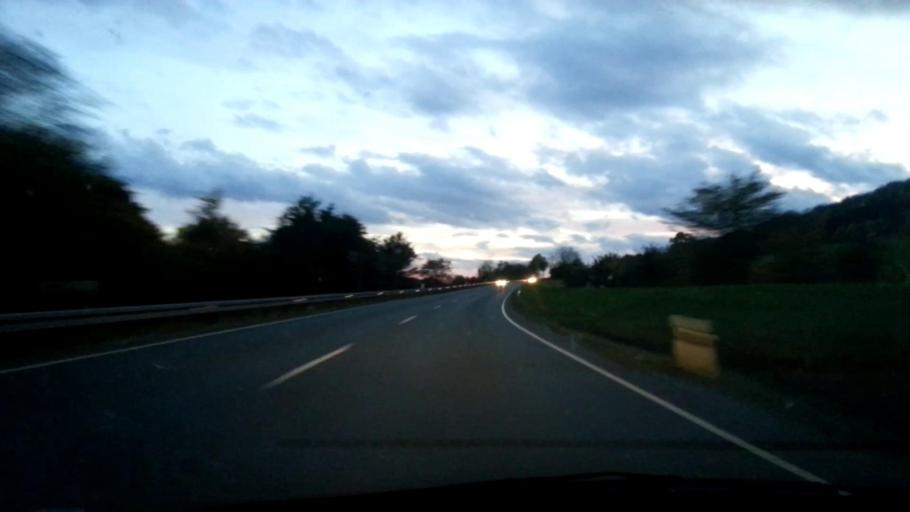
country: DE
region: Bavaria
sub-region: Upper Franconia
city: Reuth
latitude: 49.9653
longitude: 11.6613
